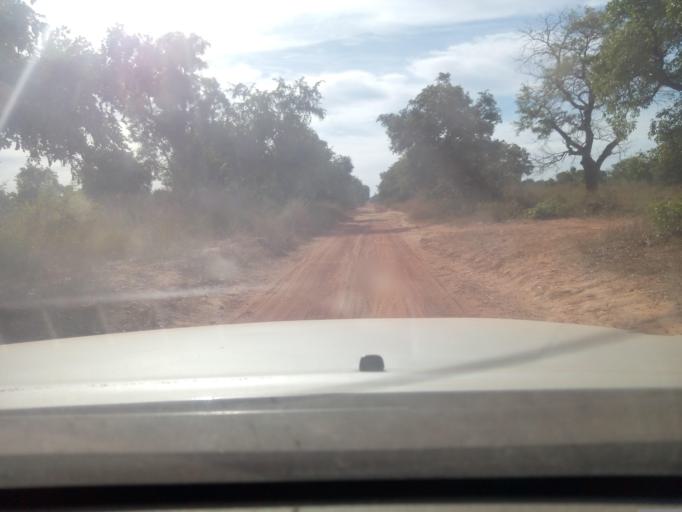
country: ML
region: Sikasso
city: Sikasso
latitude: 11.9290
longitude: -6.0715
